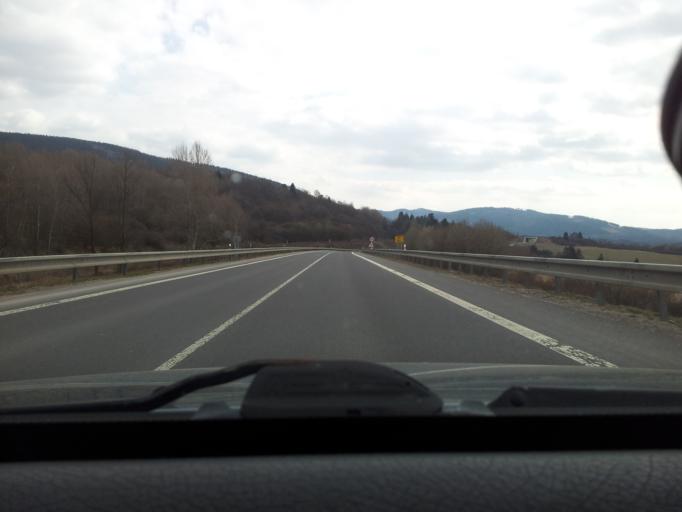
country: SK
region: Banskobystricky
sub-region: Okres Ziar nad Hronom
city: Kremnica
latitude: 48.8127
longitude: 18.8802
